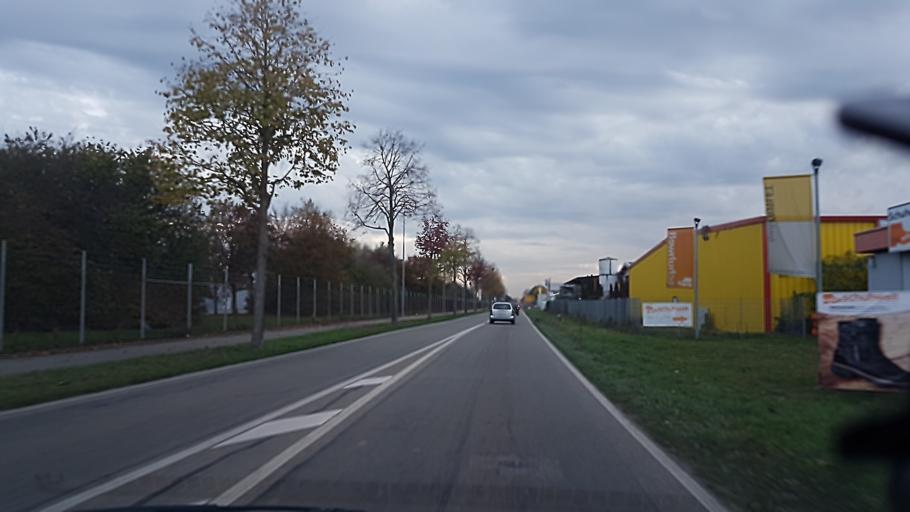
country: DE
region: Baden-Wuerttemberg
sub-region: Freiburg Region
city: Herbolzheim
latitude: 48.2210
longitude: 7.7603
